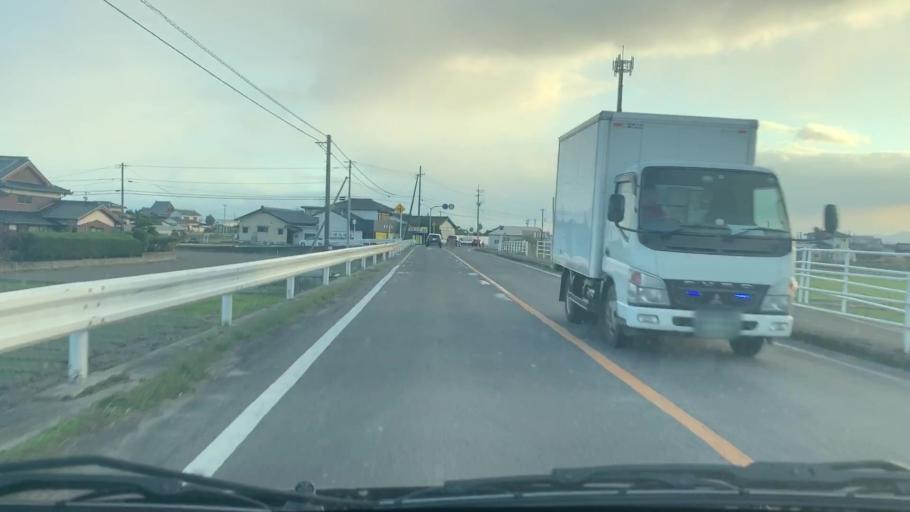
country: JP
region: Saga Prefecture
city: Saga-shi
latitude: 33.1890
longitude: 130.1930
